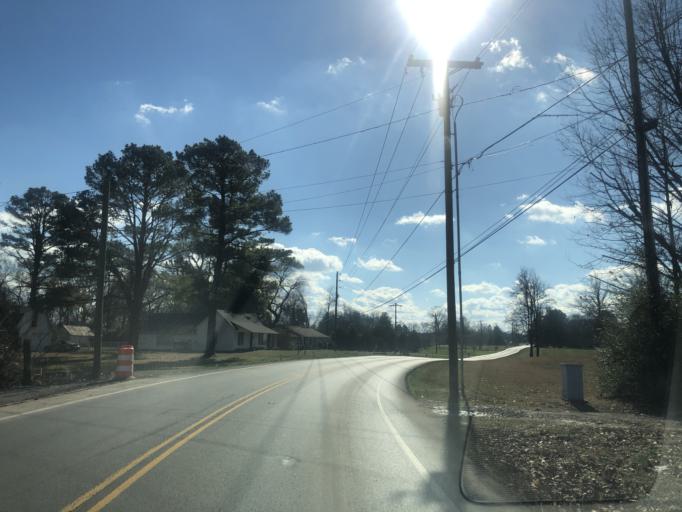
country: US
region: Tennessee
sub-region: Rutherford County
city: Smyrna
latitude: 35.8792
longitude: -86.4966
